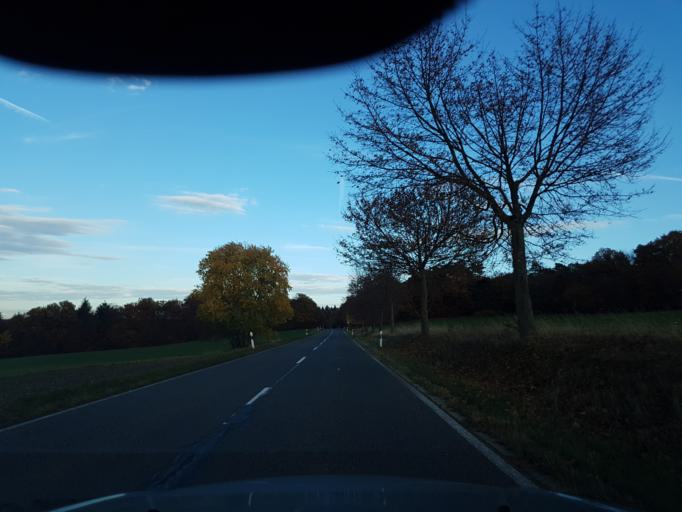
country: DE
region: Hesse
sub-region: Regierungsbezirk Darmstadt
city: Bad Schwalbach
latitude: 50.1210
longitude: 8.0192
